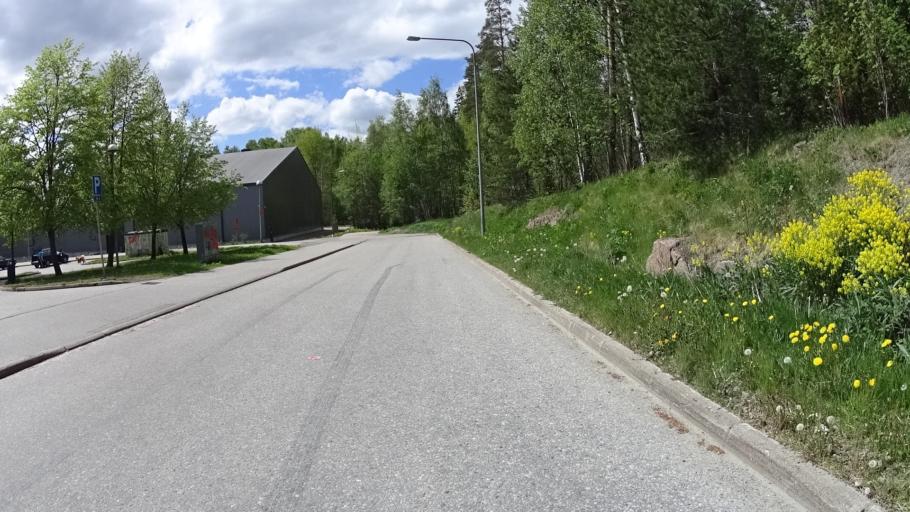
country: FI
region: Uusimaa
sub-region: Helsinki
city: Kauniainen
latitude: 60.1808
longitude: 24.7348
